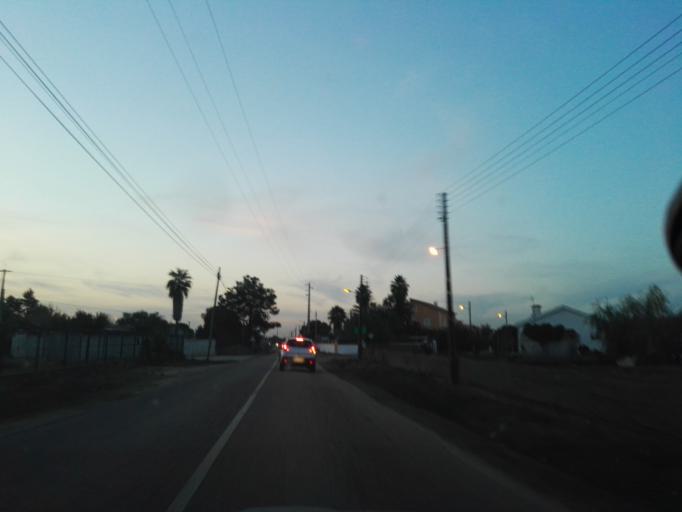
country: PT
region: Santarem
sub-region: Benavente
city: Benavente
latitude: 38.9400
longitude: -8.7989
